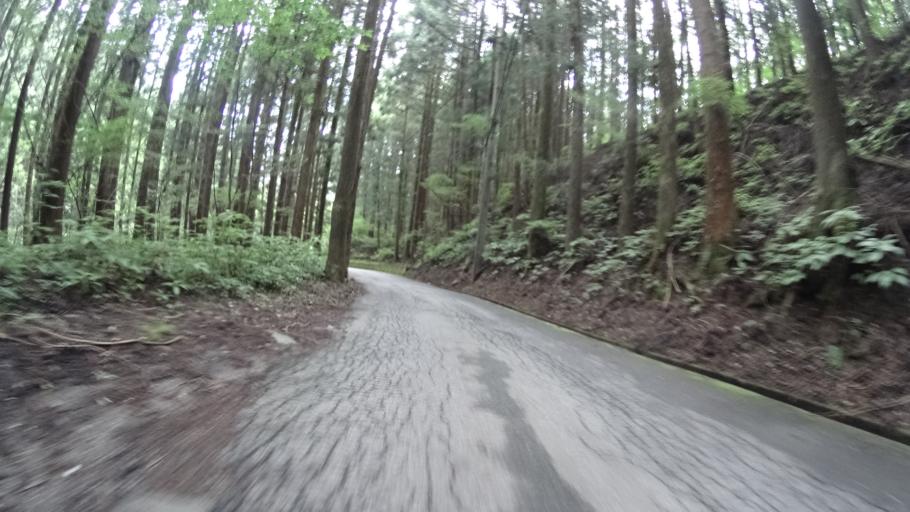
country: JP
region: Yamanashi
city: Nirasaki
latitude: 35.7912
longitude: 138.5297
